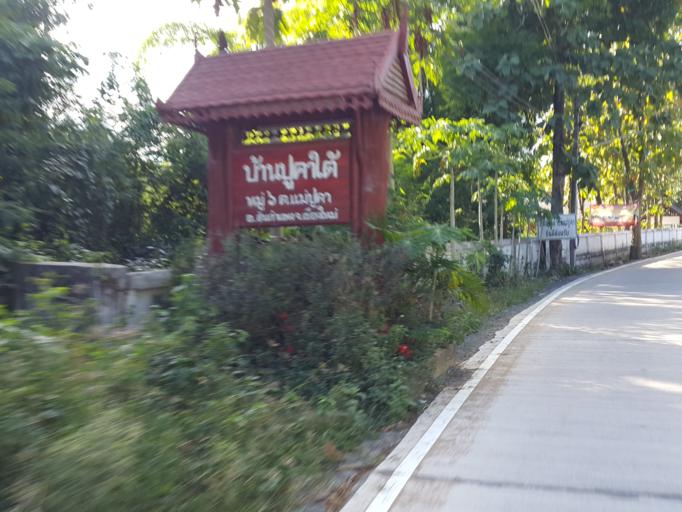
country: TH
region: Chiang Mai
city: San Kamphaeng
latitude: 18.7632
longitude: 99.1154
